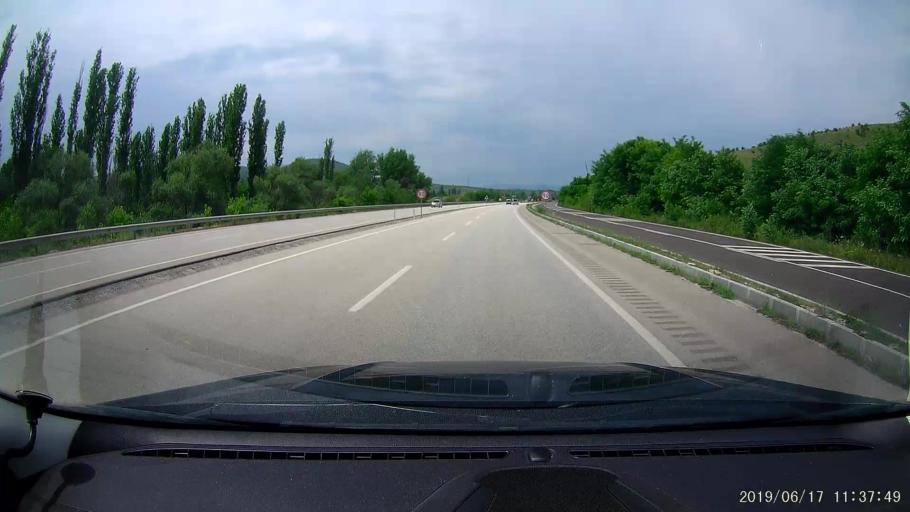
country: TR
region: Cankiri
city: Beloren
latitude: 40.8499
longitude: 33.4131
